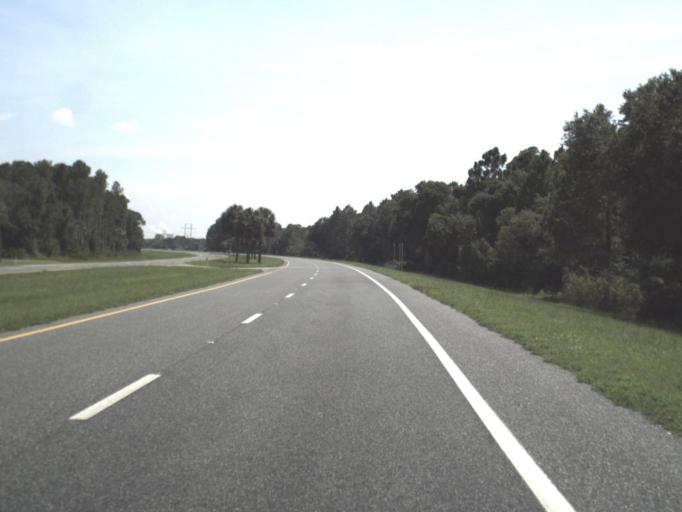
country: US
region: Florida
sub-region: Levy County
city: Inglis
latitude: 29.0436
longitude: -82.6663
